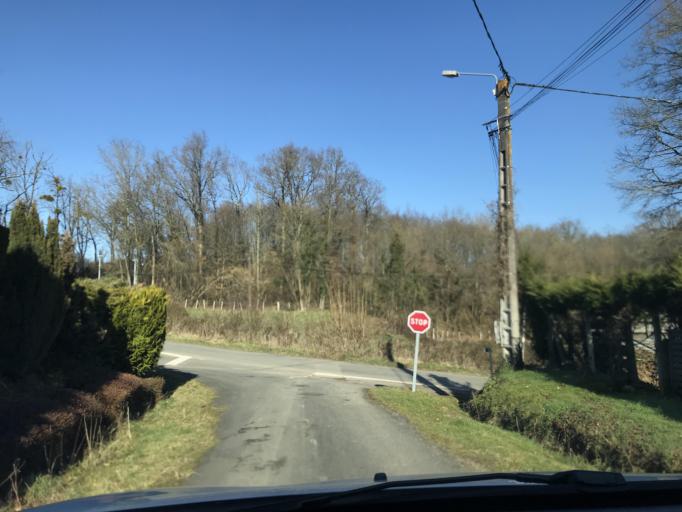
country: FR
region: Poitou-Charentes
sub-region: Departement de la Charente
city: Saint-Claud
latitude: 45.8472
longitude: 0.5050
